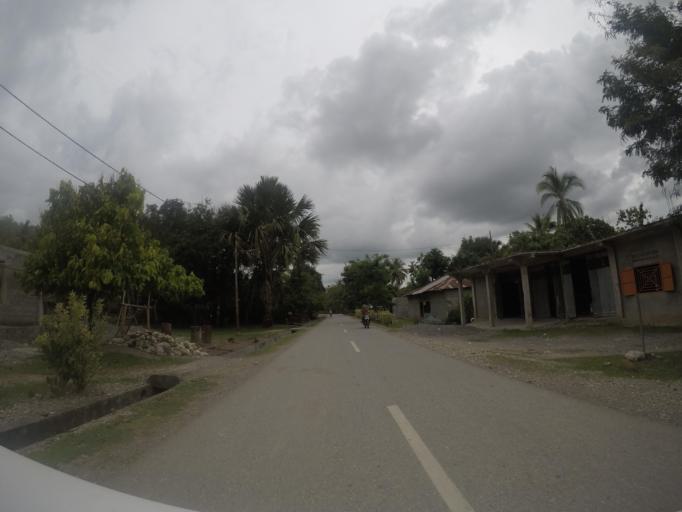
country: TL
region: Viqueque
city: Viqueque
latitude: -8.8646
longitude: 126.3673
